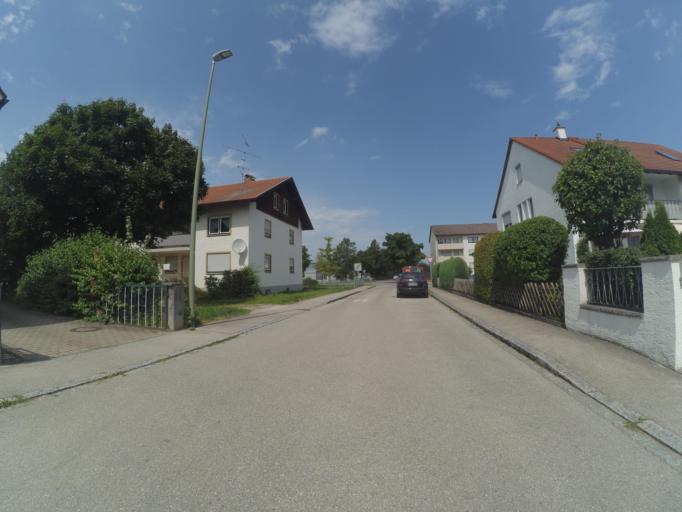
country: DE
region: Bavaria
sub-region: Swabia
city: Buchloe
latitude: 48.0389
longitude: 10.7114
